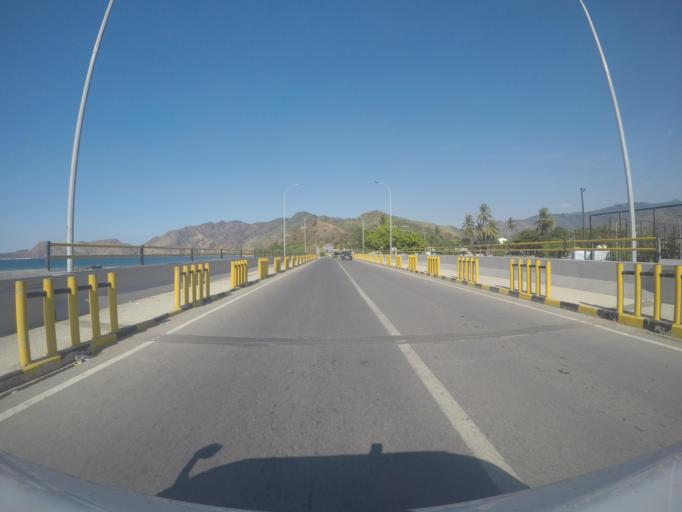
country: TL
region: Dili
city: Dili
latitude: -8.5479
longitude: 125.5905
